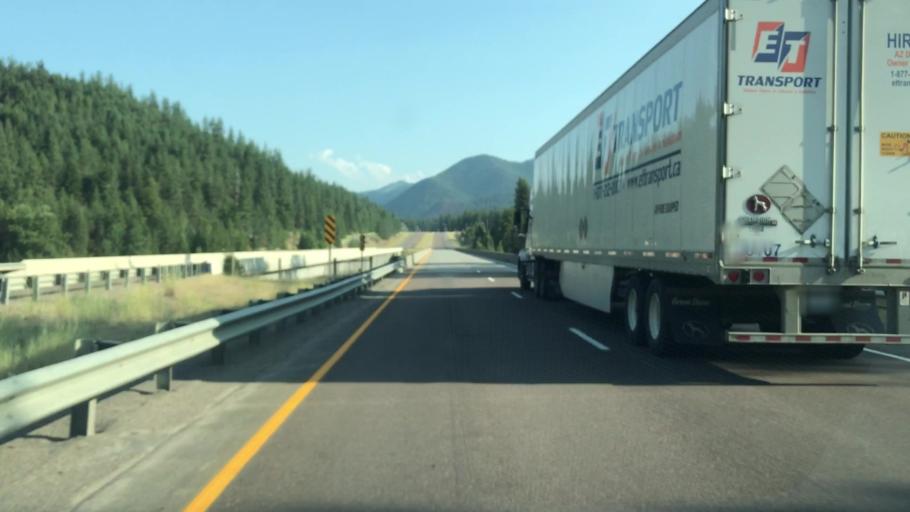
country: US
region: Montana
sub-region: Mineral County
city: Superior
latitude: 47.0699
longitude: -114.7650
